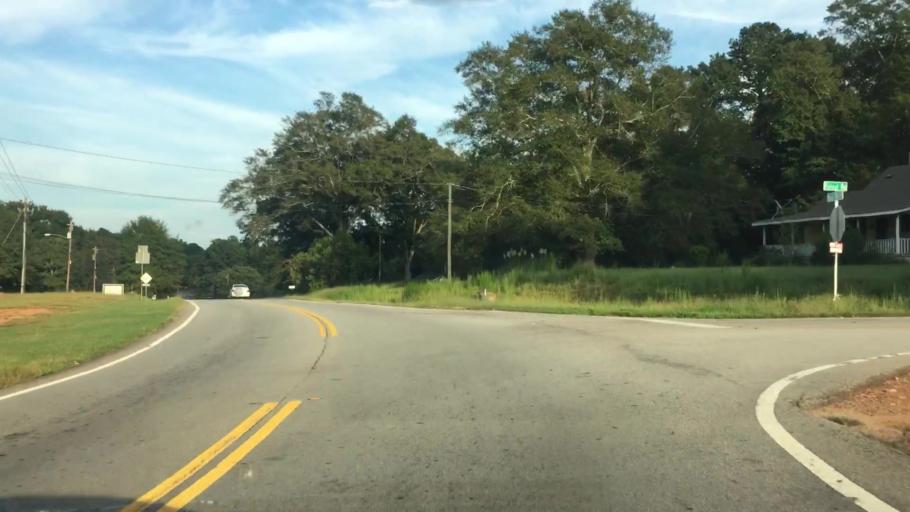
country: US
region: Georgia
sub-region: Henry County
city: Stockbridge
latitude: 33.5405
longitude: -84.1936
